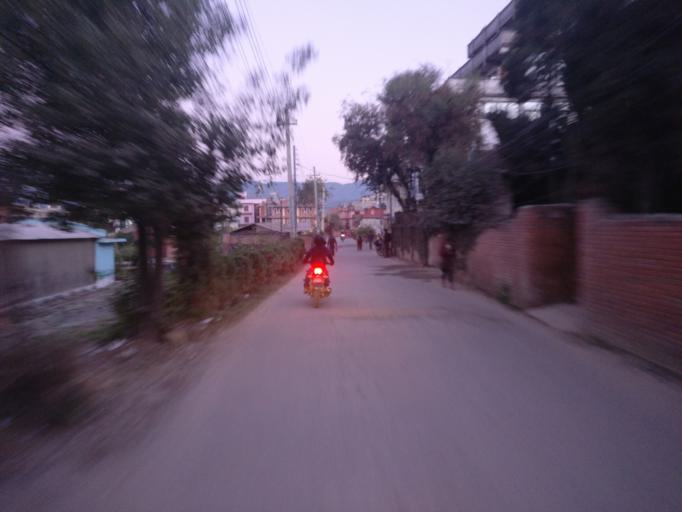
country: NP
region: Central Region
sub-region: Bagmati Zone
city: Patan
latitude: 27.6497
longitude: 85.3225
